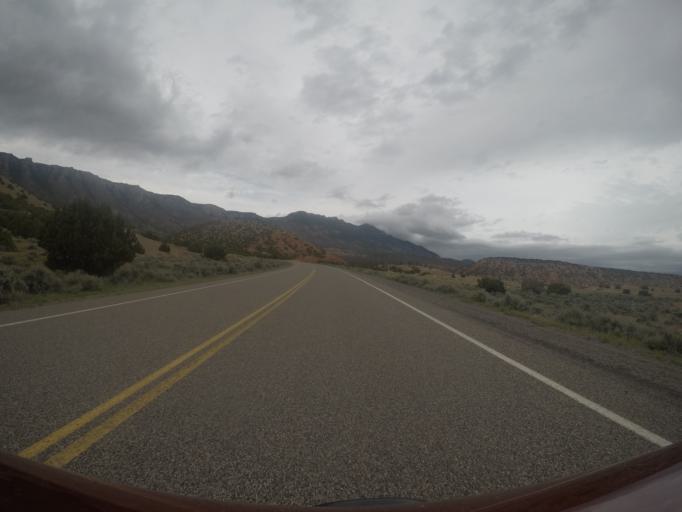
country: US
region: Wyoming
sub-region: Big Horn County
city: Lovell
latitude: 45.0728
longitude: -108.2558
